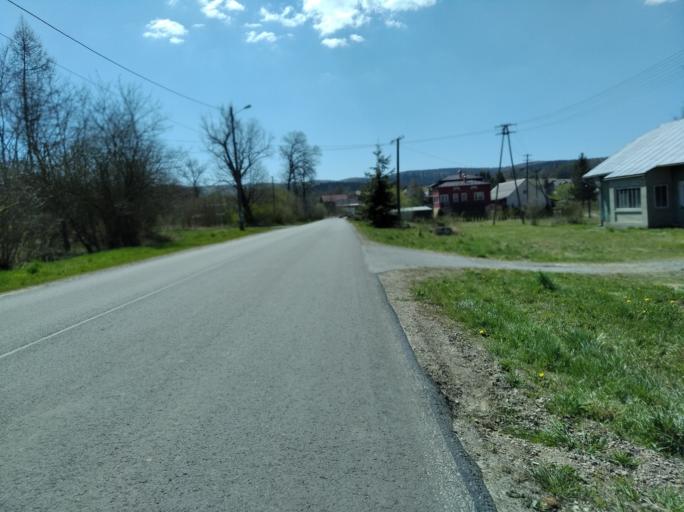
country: PL
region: Subcarpathian Voivodeship
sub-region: Powiat brzozowski
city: Dydnia
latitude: 49.6842
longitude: 22.1867
